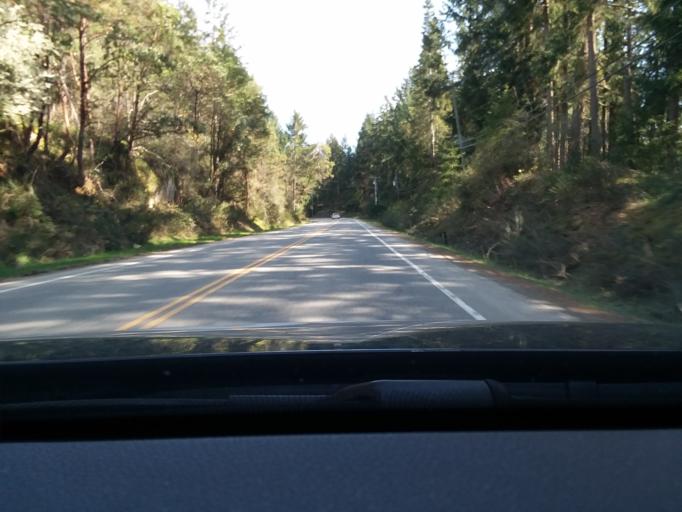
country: CA
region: British Columbia
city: North Saanich
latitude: 48.8545
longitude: -123.4730
